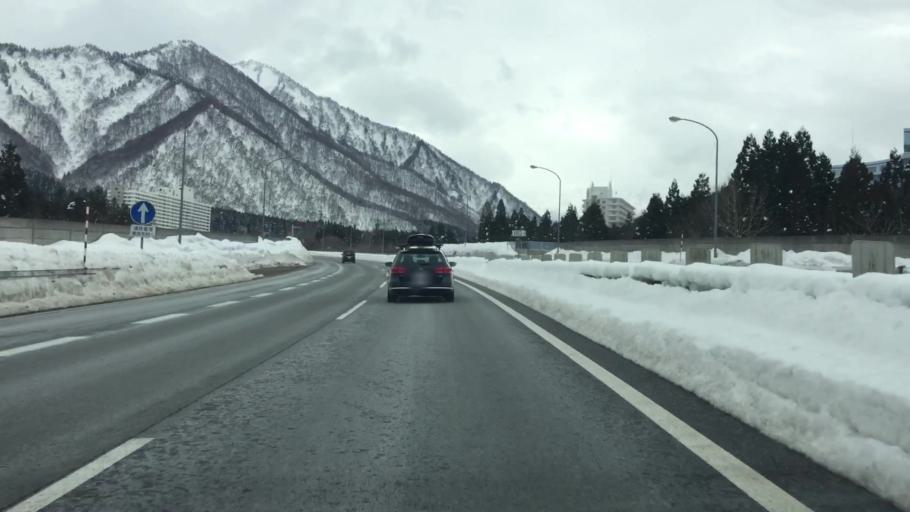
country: JP
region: Niigata
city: Shiozawa
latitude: 36.9090
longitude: 138.8414
